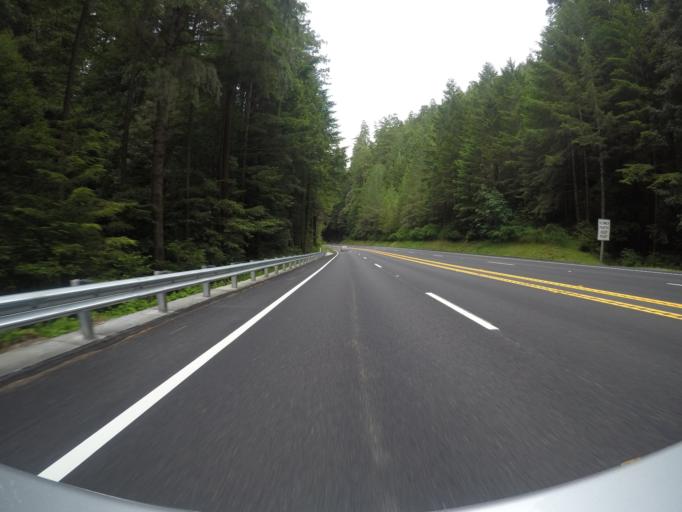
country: US
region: California
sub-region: Humboldt County
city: Rio Dell
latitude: 40.3418
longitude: -123.9329
